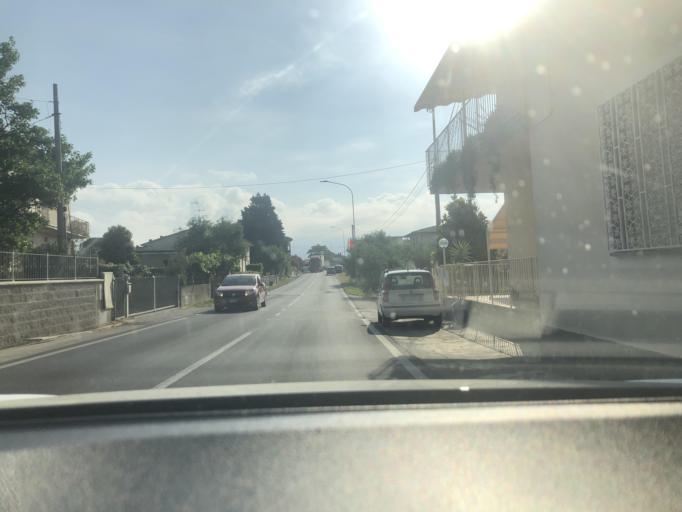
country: IT
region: Tuscany
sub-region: Provincia di Pistoia
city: Lamporecchio
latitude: 43.8061
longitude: 10.8614
